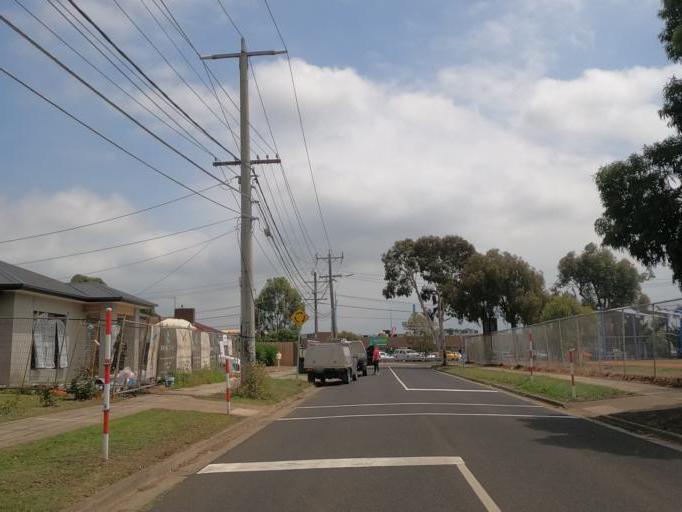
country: AU
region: Victoria
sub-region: Hume
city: Gladstone Park
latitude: -37.6885
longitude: 144.8871
